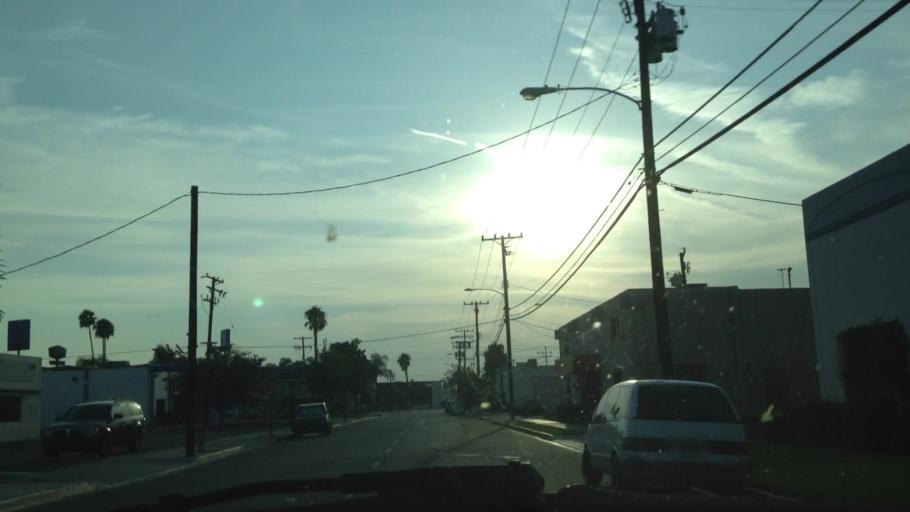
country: US
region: California
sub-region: Orange County
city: Placentia
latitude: 33.8562
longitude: -117.8865
